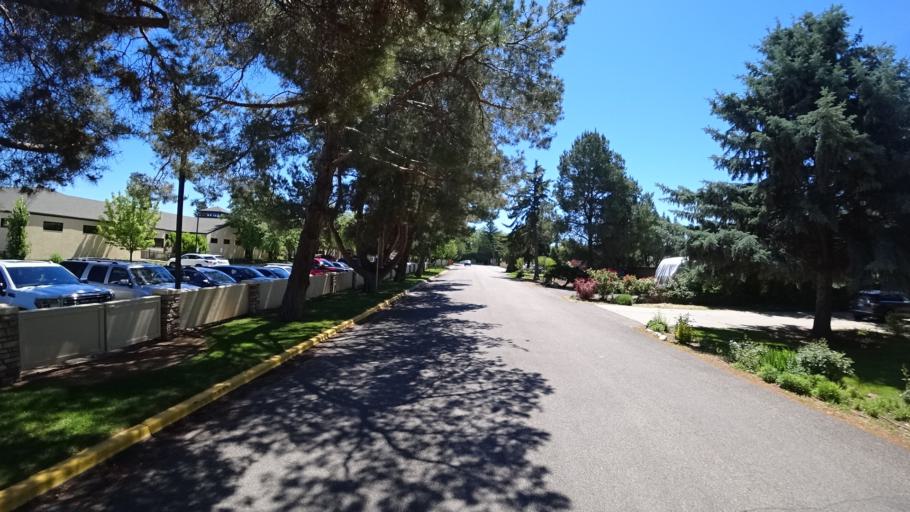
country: US
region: Idaho
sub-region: Ada County
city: Garden City
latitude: 43.5858
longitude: -116.2406
